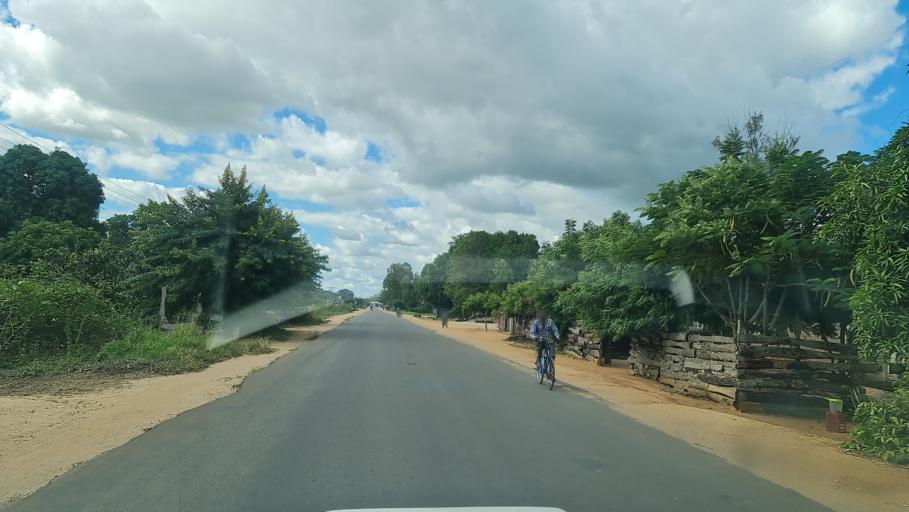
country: MZ
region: Zambezia
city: Quelimane
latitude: -17.5999
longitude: 36.8064
